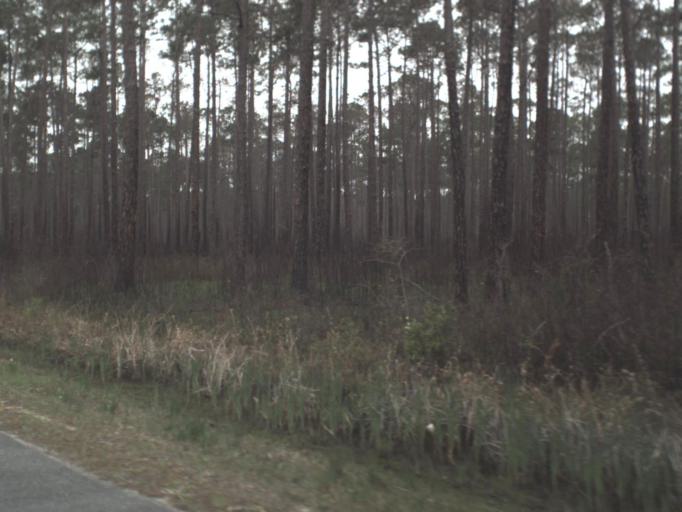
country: US
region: Florida
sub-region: Franklin County
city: Apalachicola
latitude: 29.9418
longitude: -84.9767
